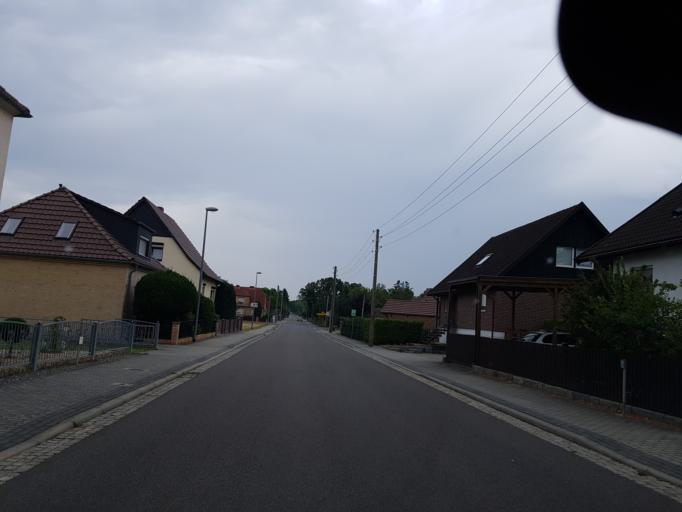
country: DE
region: Brandenburg
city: Schipkau
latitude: 51.5506
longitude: 13.9198
